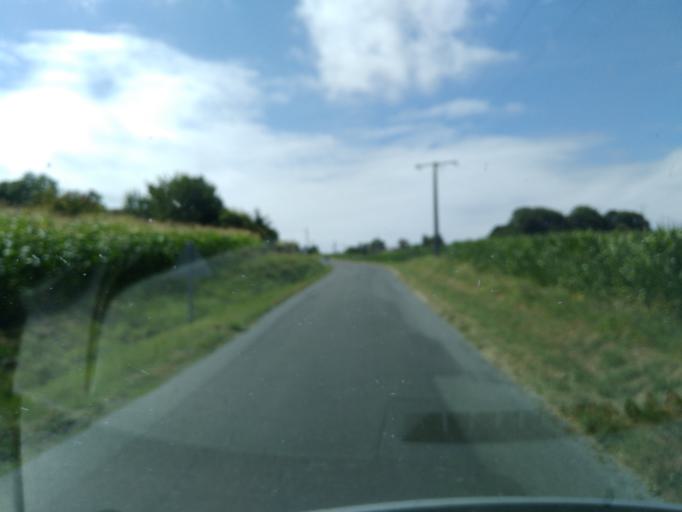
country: FR
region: Poitou-Charentes
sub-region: Departement de la Charente-Maritime
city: Saint-Palais-sur-Mer
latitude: 45.6784
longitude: -1.0871
